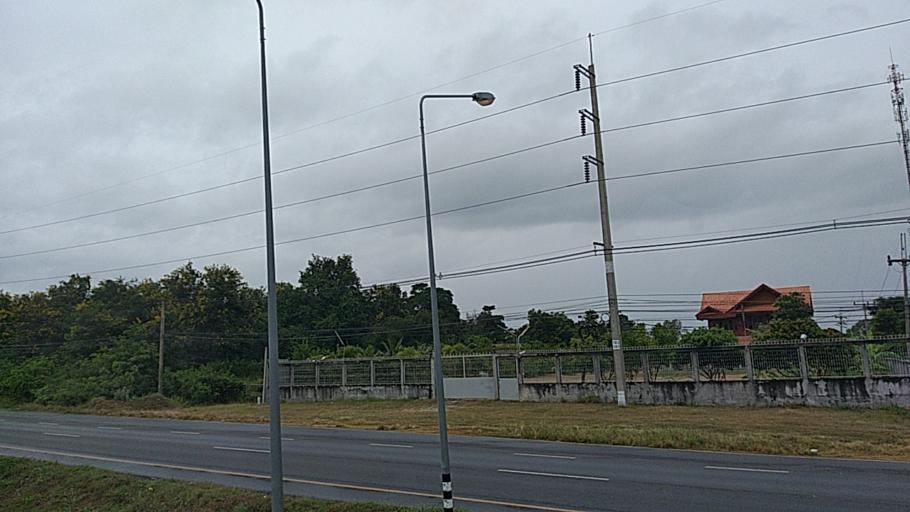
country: TH
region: Maha Sarakham
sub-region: Amphoe Borabue
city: Borabue
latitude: 16.0610
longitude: 103.1387
